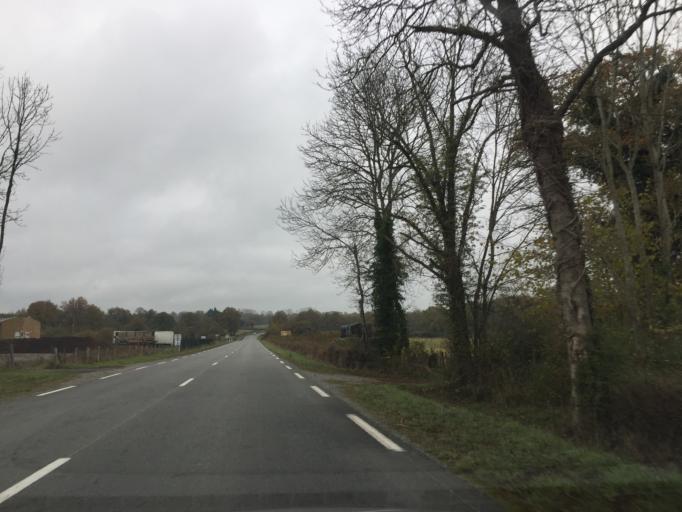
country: FR
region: Limousin
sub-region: Departement de la Creuse
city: Gouzon
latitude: 46.1273
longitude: 2.1883
